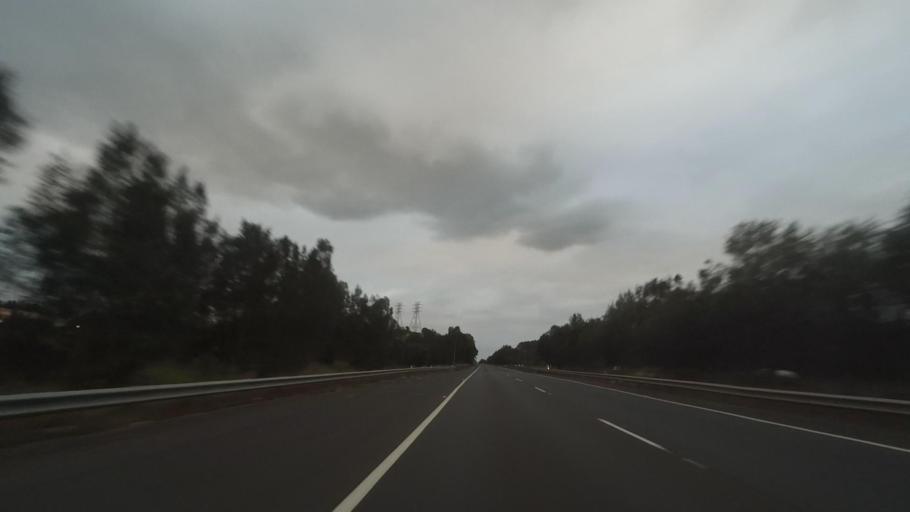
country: AU
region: New South Wales
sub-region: Wollongong
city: Berkeley
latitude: -34.4743
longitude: 150.8310
